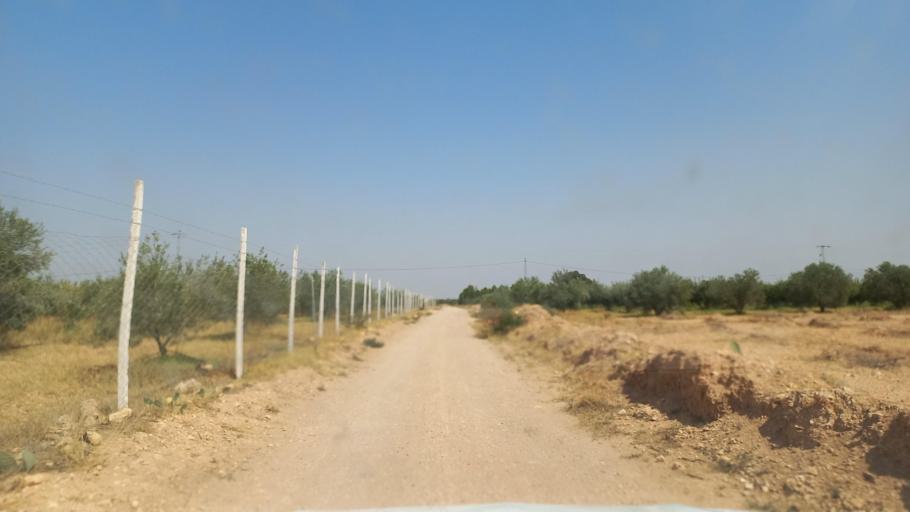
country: TN
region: Al Qasrayn
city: Kasserine
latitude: 35.2492
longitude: 9.0130
